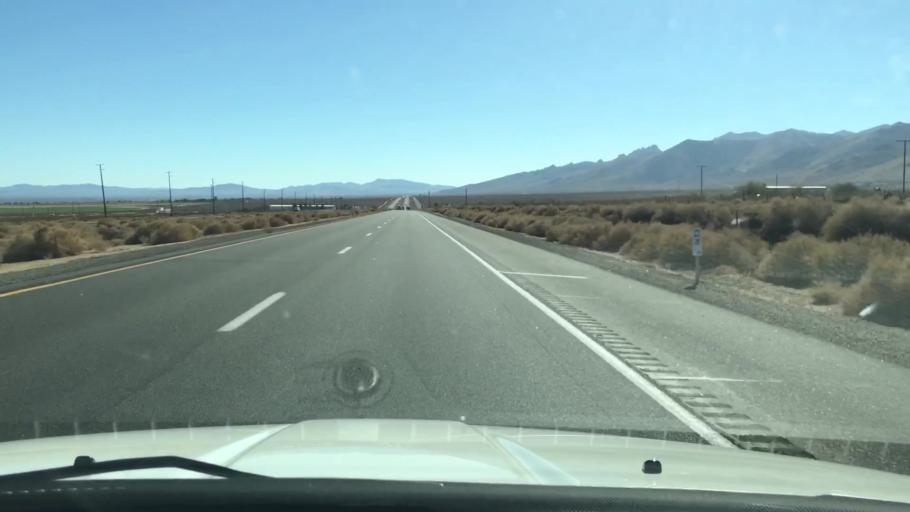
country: US
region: California
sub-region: Kern County
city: Inyokern
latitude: 35.8128
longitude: -117.8737
